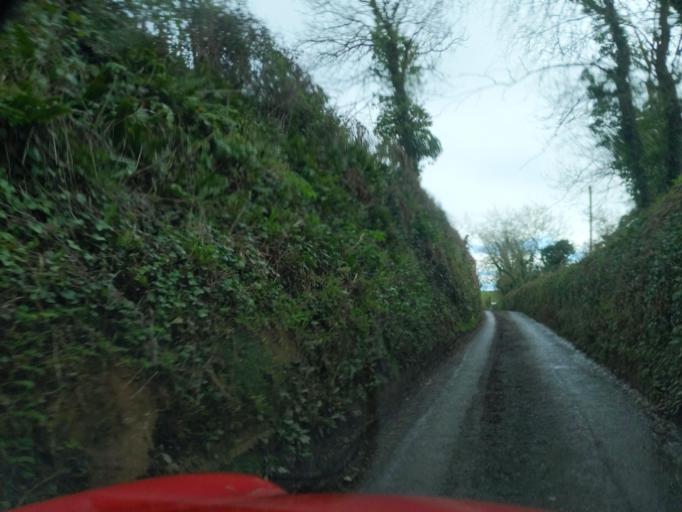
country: GB
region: England
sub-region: Devon
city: Salcombe
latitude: 50.2684
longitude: -3.6940
